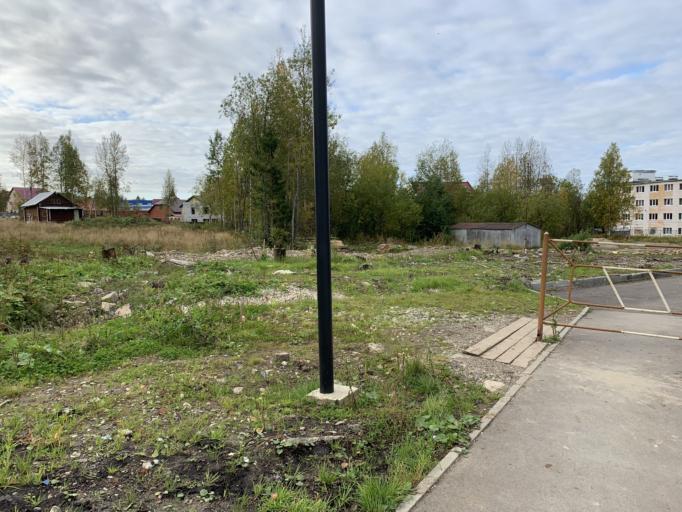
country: RU
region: Perm
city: Gubakha
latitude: 58.8321
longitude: 57.5618
